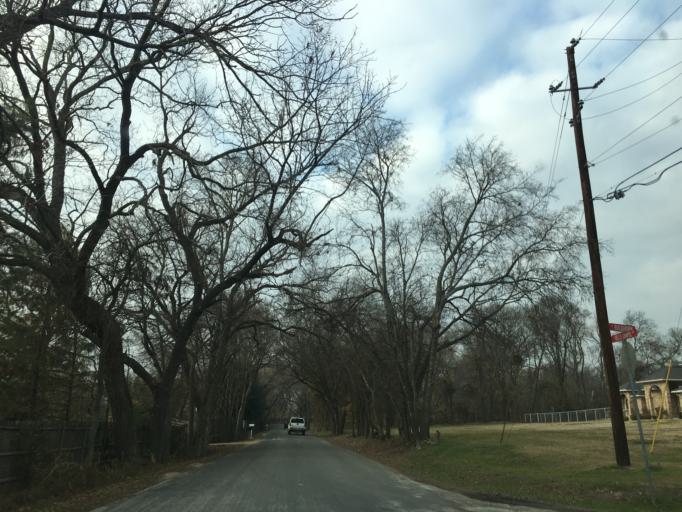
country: US
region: Texas
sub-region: Ellis County
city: Red Oak
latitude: 32.4896
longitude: -96.7997
